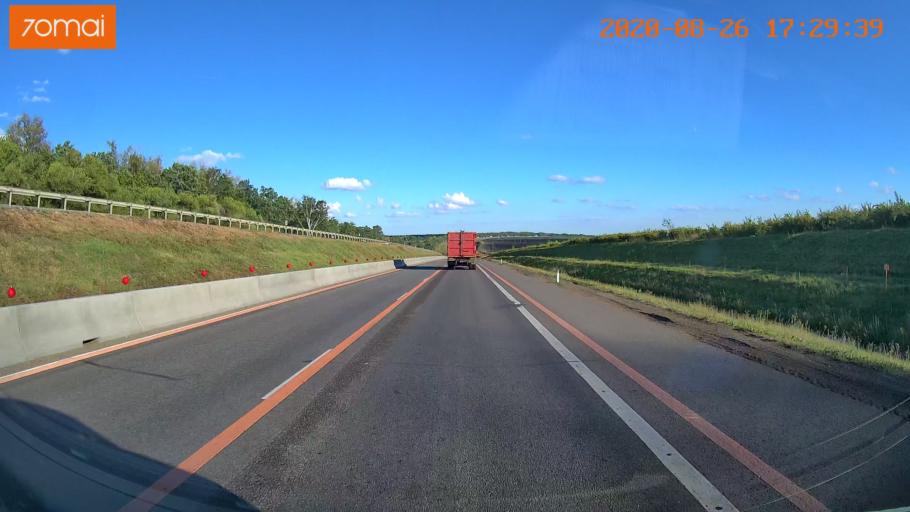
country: RU
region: Tula
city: Kazachka
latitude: 53.4523
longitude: 38.1551
